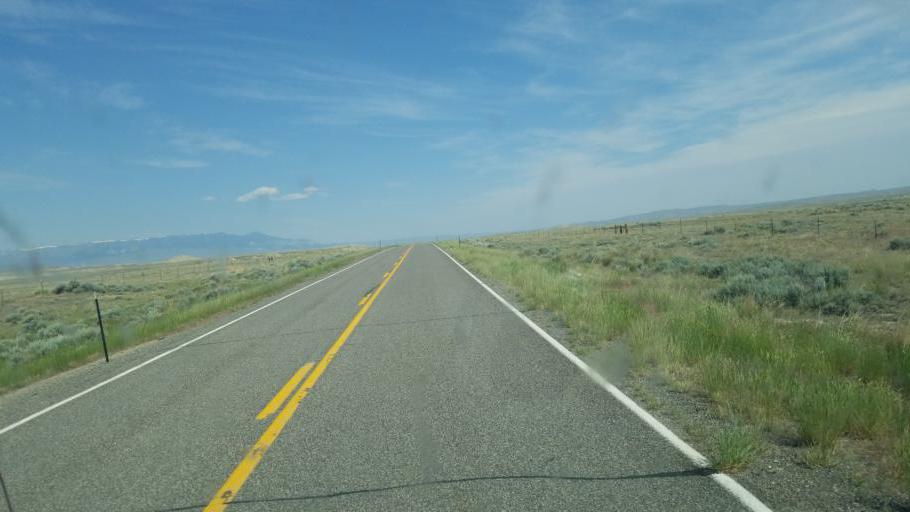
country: US
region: Wyoming
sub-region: Park County
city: Powell
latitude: 44.8117
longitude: -108.9682
